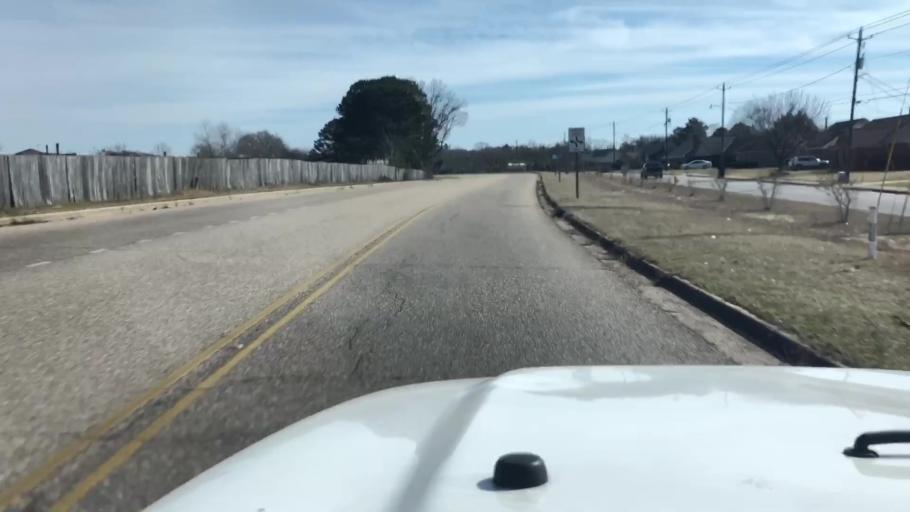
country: US
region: Alabama
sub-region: Elmore County
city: Blue Ridge
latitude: 32.4050
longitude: -86.1793
